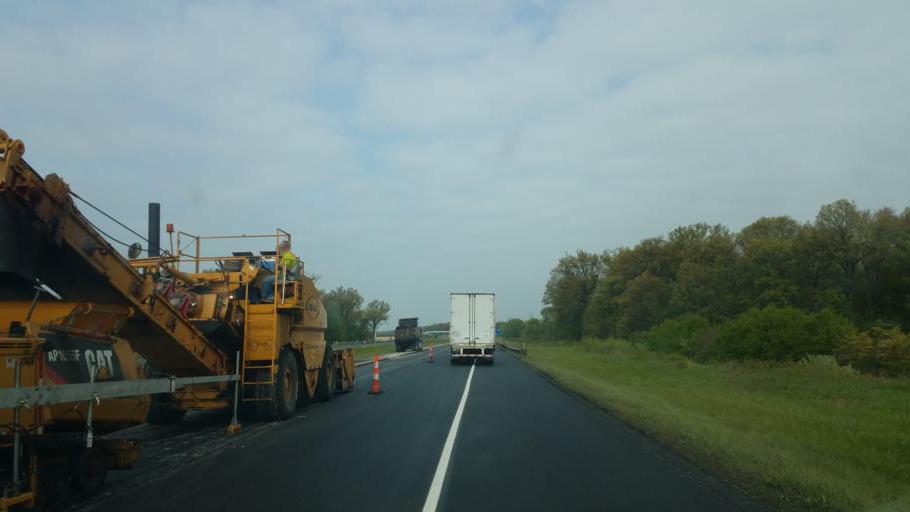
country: US
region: Indiana
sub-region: Saint Joseph County
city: Granger
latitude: 41.7321
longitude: -86.0965
